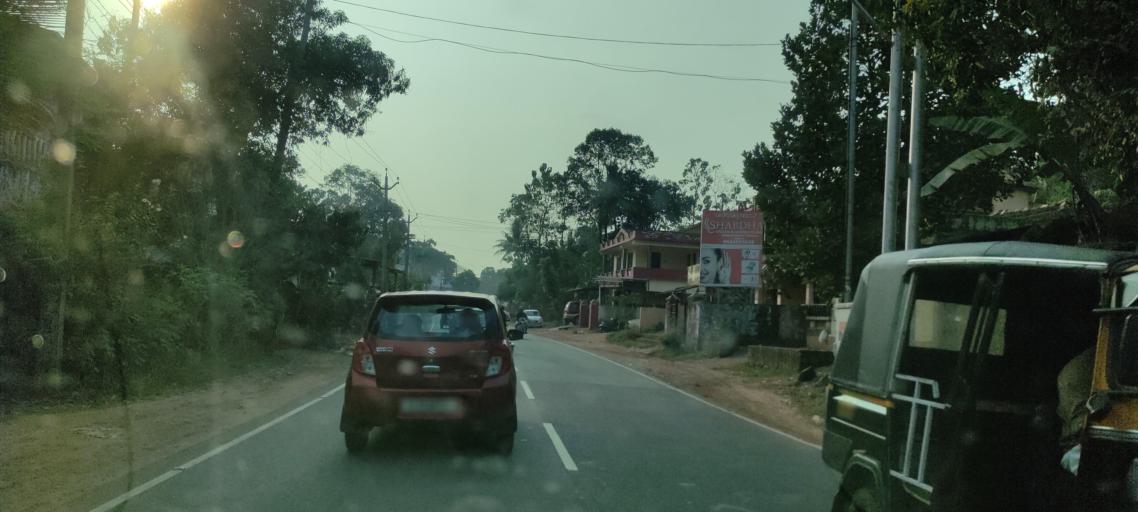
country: IN
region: Kerala
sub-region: Pattanamtitta
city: Adur
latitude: 9.1671
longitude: 76.6730
